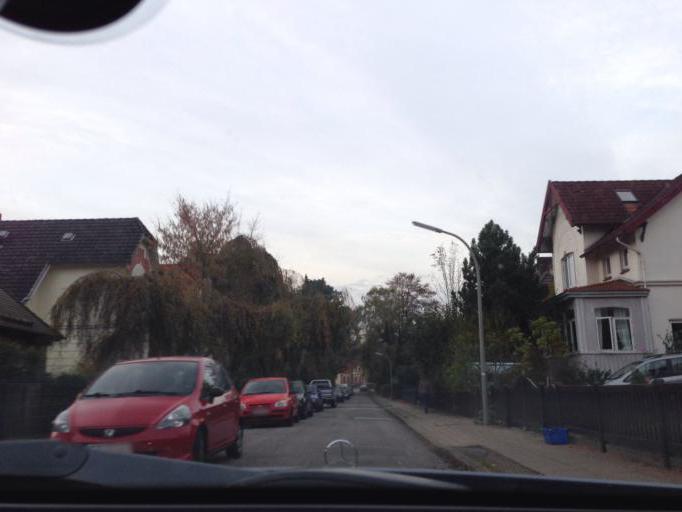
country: DE
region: Schleswig-Holstein
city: Barsbuettel
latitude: 53.6020
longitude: 10.1615
